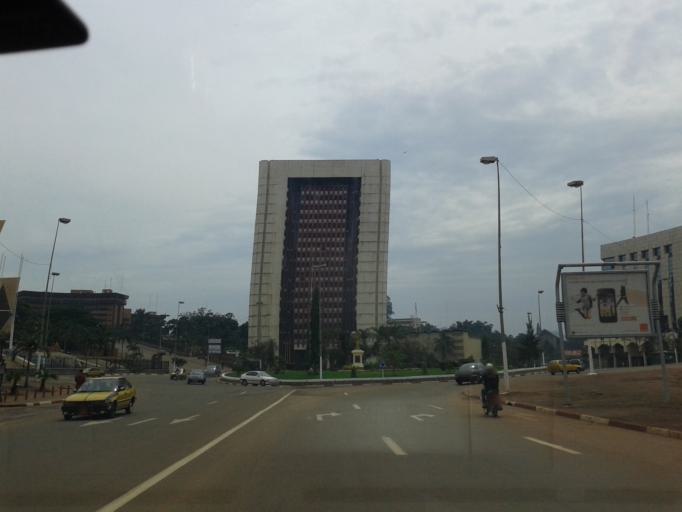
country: CM
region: Centre
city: Yaounde
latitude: 3.8655
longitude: 11.5160
